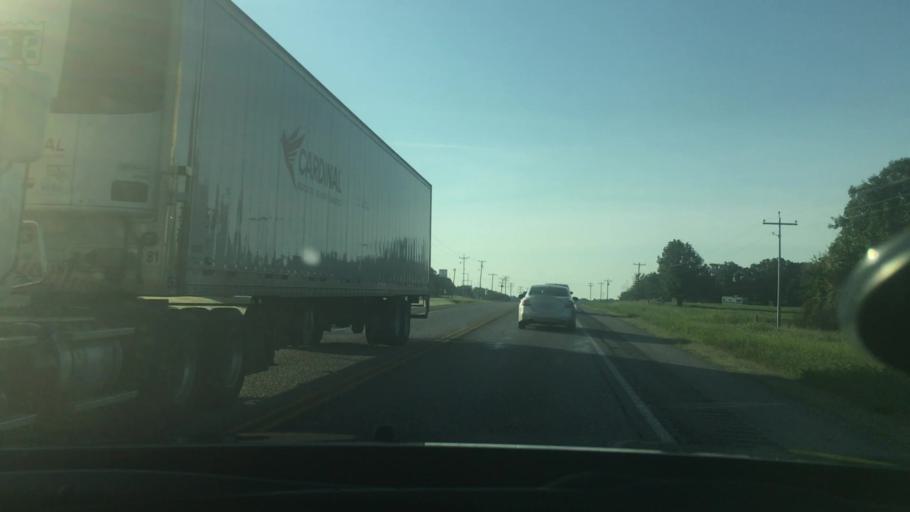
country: US
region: Oklahoma
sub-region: Pontotoc County
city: Ada
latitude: 34.8021
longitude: -96.7428
